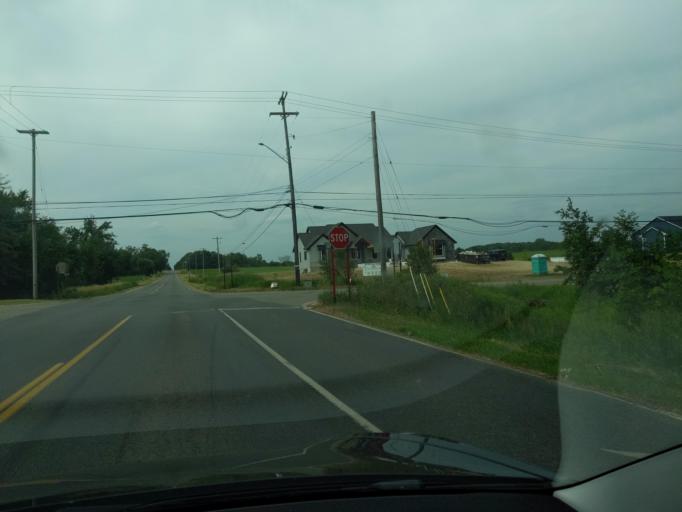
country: US
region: Michigan
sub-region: Clinton County
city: DeWitt
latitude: 42.8419
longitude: -84.6025
